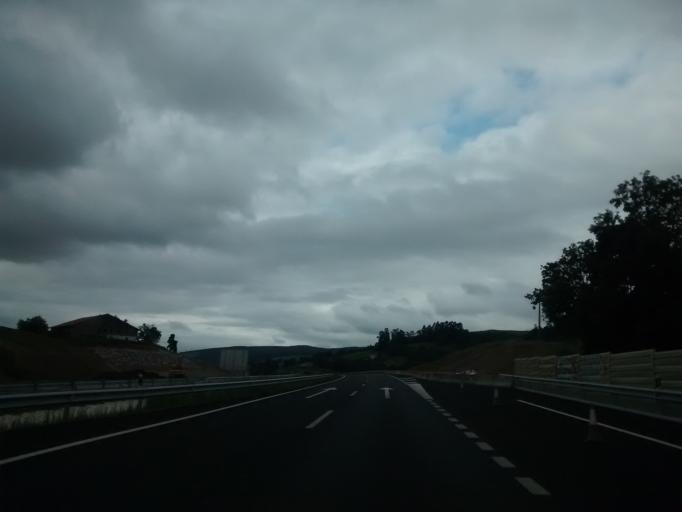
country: ES
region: Cantabria
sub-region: Provincia de Cantabria
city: Penagos
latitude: 43.3359
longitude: -3.8195
